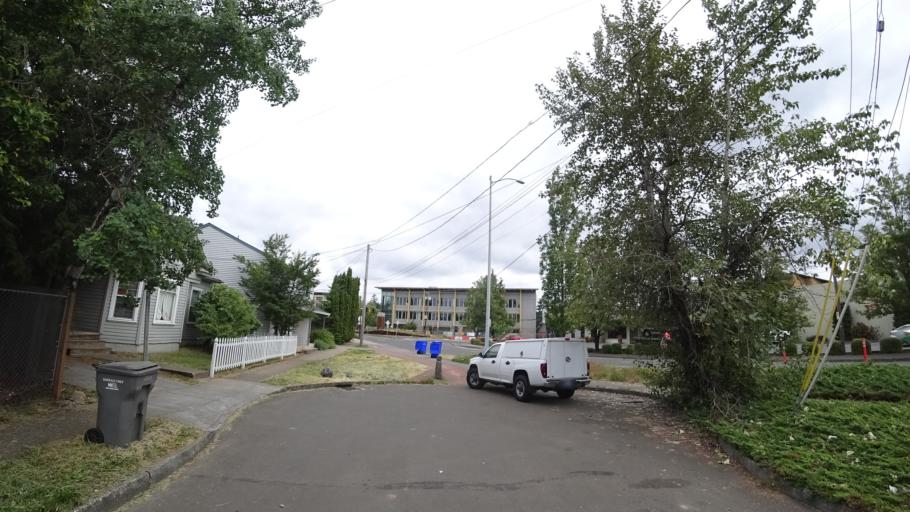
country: US
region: Oregon
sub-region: Multnomah County
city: Lents
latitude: 45.4796
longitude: -122.5707
